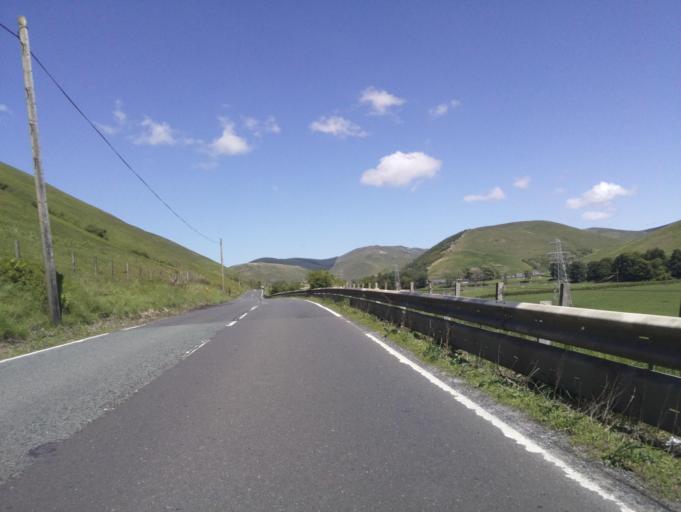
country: GB
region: Scotland
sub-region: Dumfries and Galloway
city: Langholm
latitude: 55.2381
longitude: -2.9734
